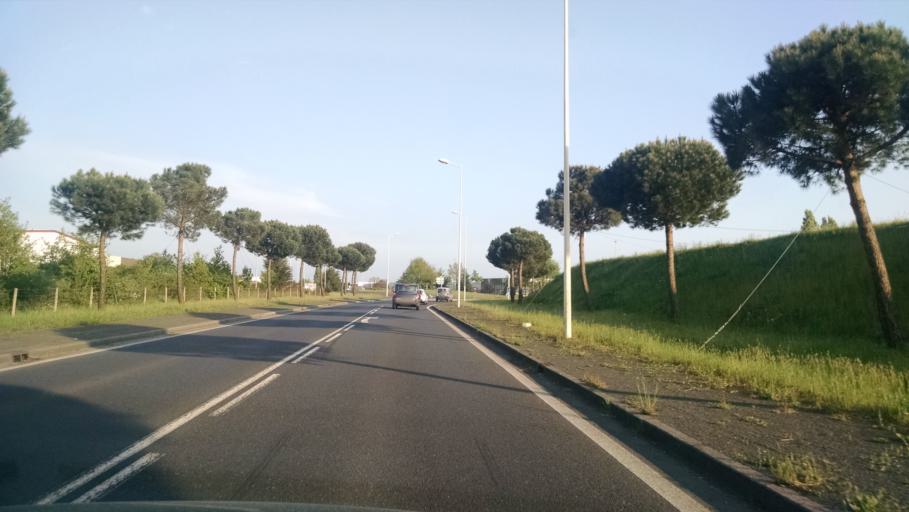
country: FR
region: Pays de la Loire
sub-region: Departement de la Loire-Atlantique
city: Getigne
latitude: 47.0848
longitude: -1.2591
